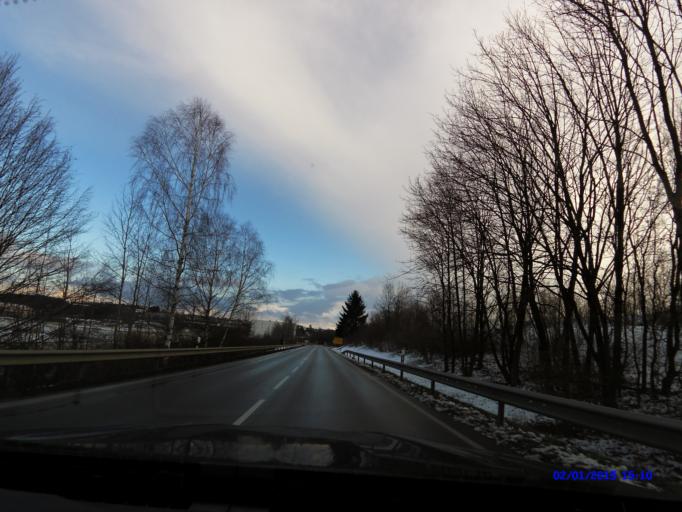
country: DE
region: Bavaria
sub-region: Lower Bavaria
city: Mainburg
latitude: 48.6305
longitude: 11.7725
